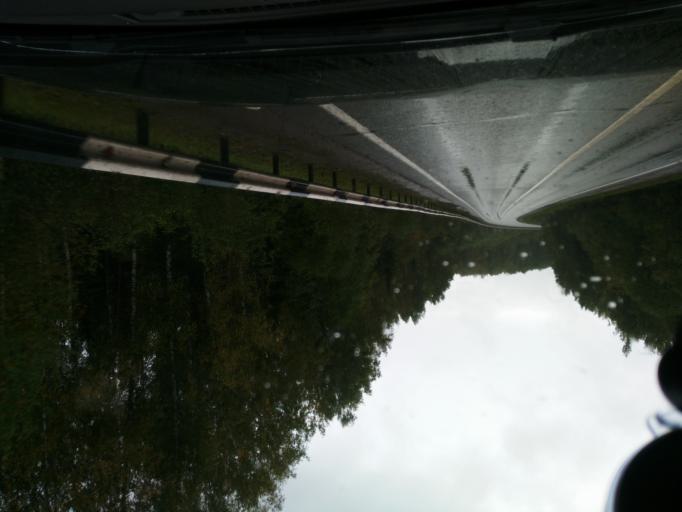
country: RU
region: Perm
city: Yugo-Kamskiy
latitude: 57.7404
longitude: 55.7114
